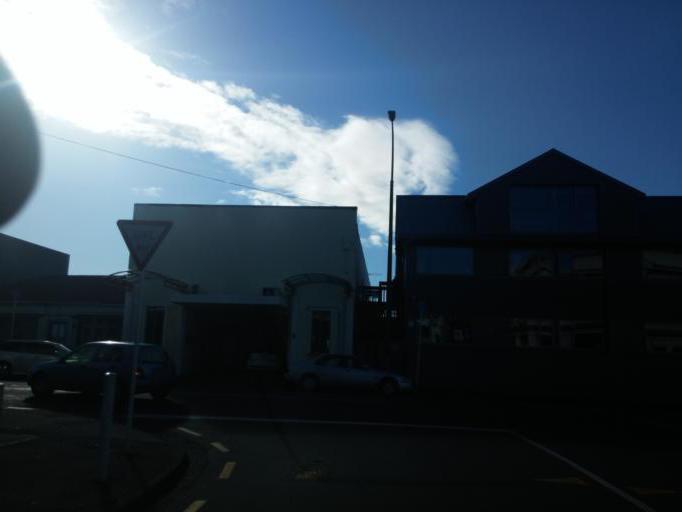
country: NZ
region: Wellington
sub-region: Wellington City
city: Wellington
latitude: -41.2983
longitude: 174.7743
